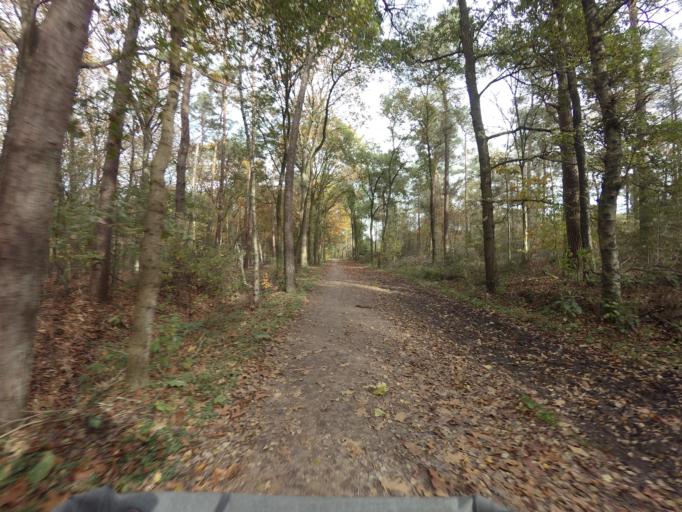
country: NL
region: North Holland
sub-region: Gemeente Hilversum
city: Hilversum
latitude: 52.1901
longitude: 5.2032
